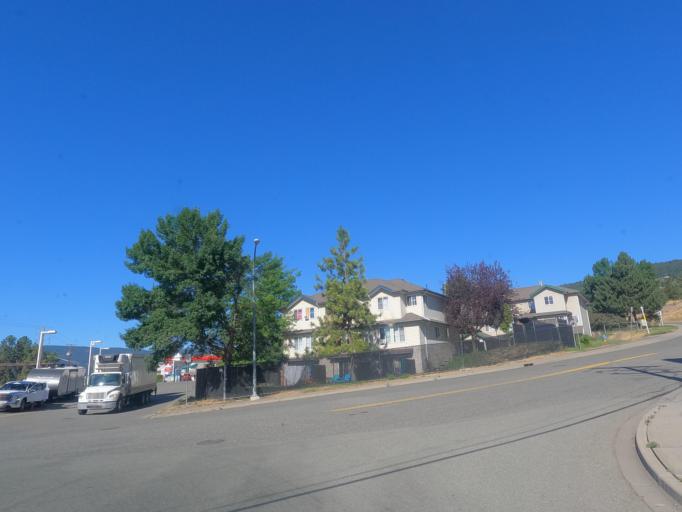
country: CA
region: British Columbia
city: Merritt
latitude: 50.1238
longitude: -120.7636
